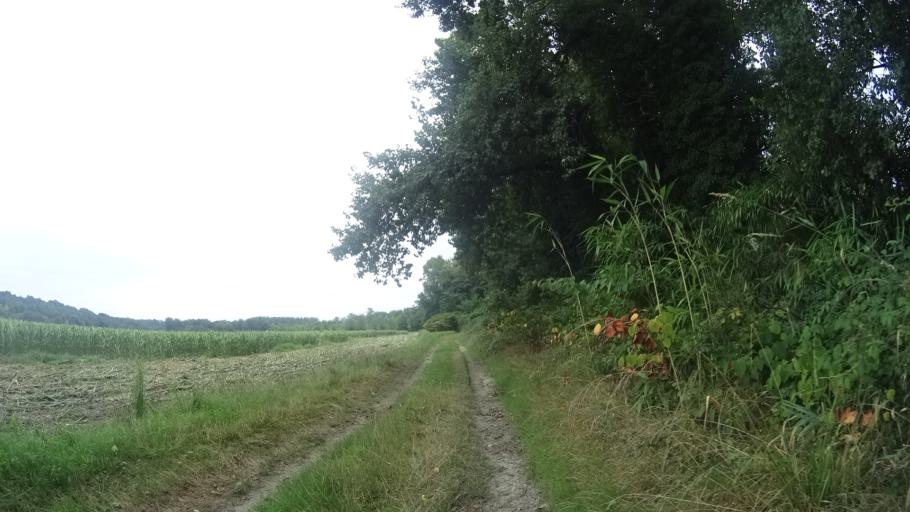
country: FR
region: Aquitaine
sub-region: Departement des Pyrenees-Atlantiques
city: Orthez
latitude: 43.4633
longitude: -0.7223
